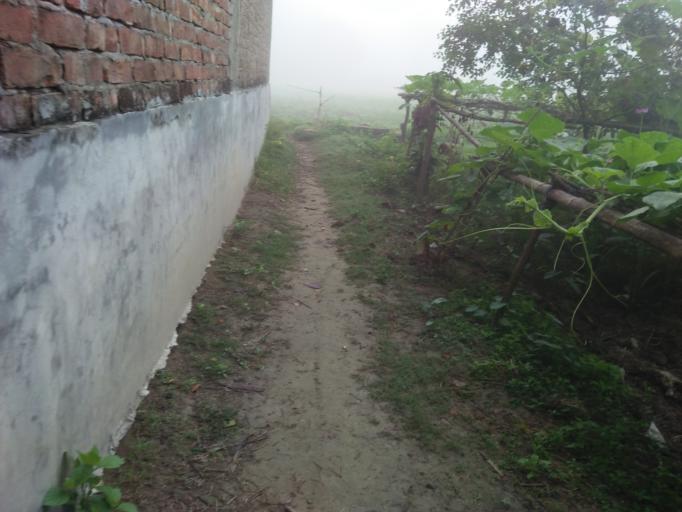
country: BD
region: Dhaka
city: Azimpur
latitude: 23.6880
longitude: 90.2971
